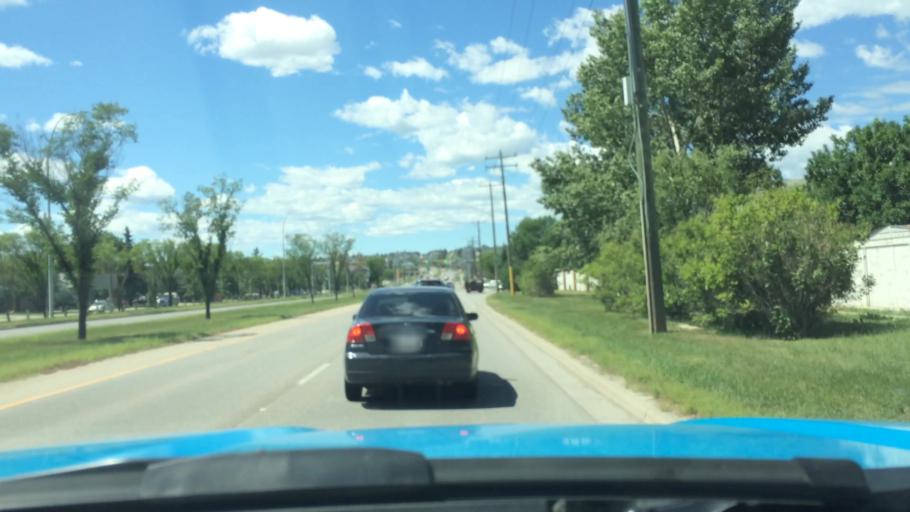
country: CA
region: Alberta
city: Calgary
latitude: 51.1543
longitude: -114.0501
